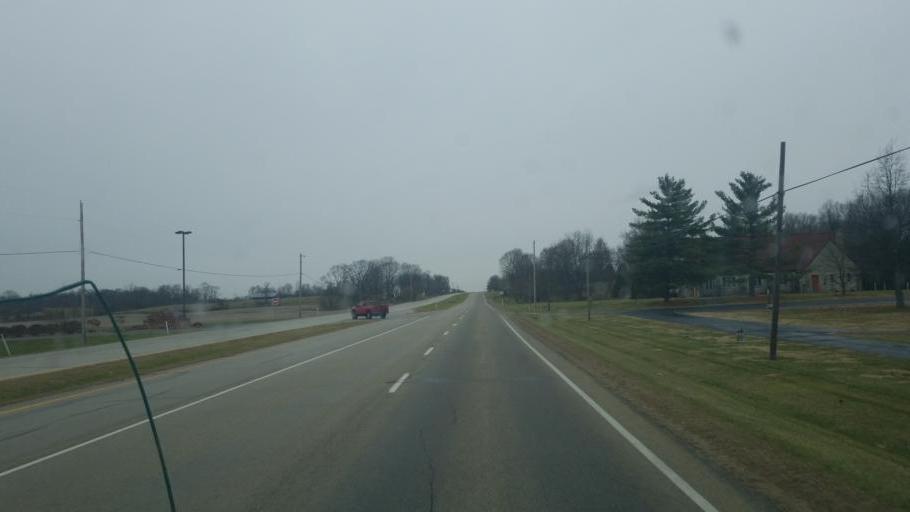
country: US
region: Indiana
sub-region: Henry County
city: Knightstown
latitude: 39.7942
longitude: -85.5425
